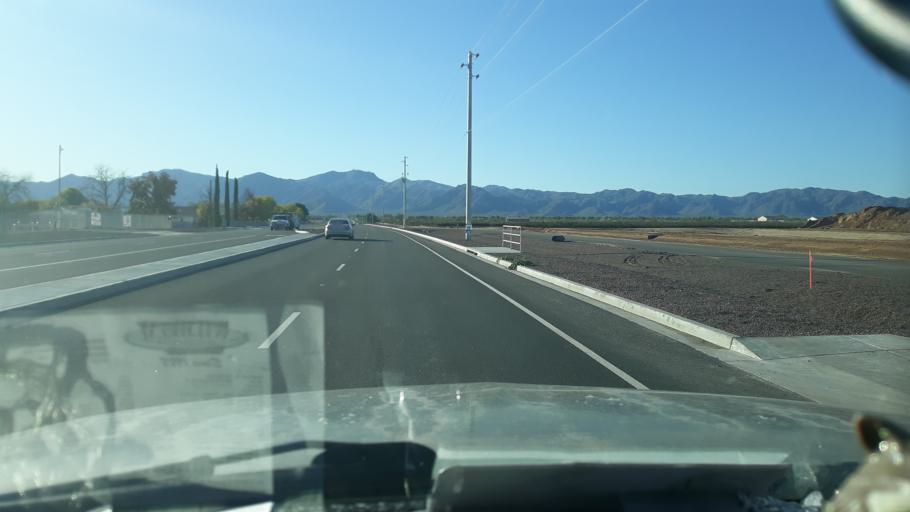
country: US
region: Arizona
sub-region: Maricopa County
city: Citrus Park
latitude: 33.5662
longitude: -112.4275
